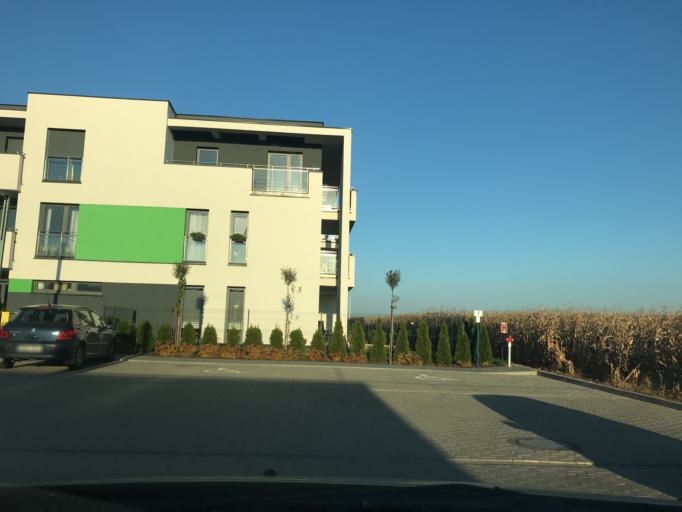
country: PL
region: Greater Poland Voivodeship
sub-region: Powiat poznanski
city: Baranowo
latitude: 52.3948
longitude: 16.7663
